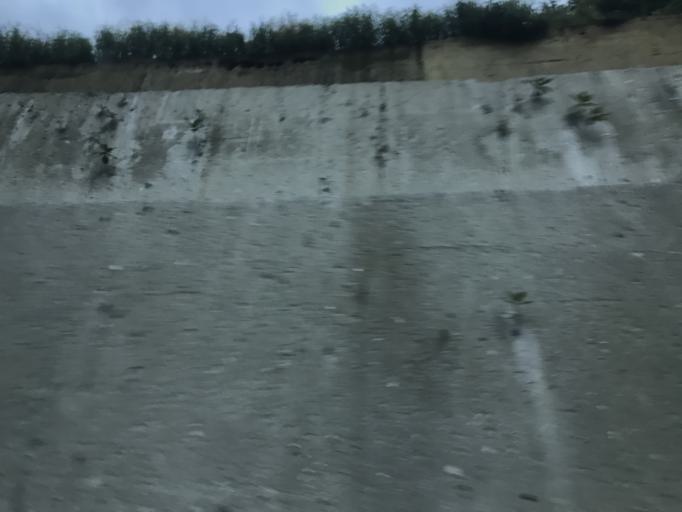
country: GT
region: Chimaltenango
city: El Tejar
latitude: 14.6387
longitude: -90.7906
